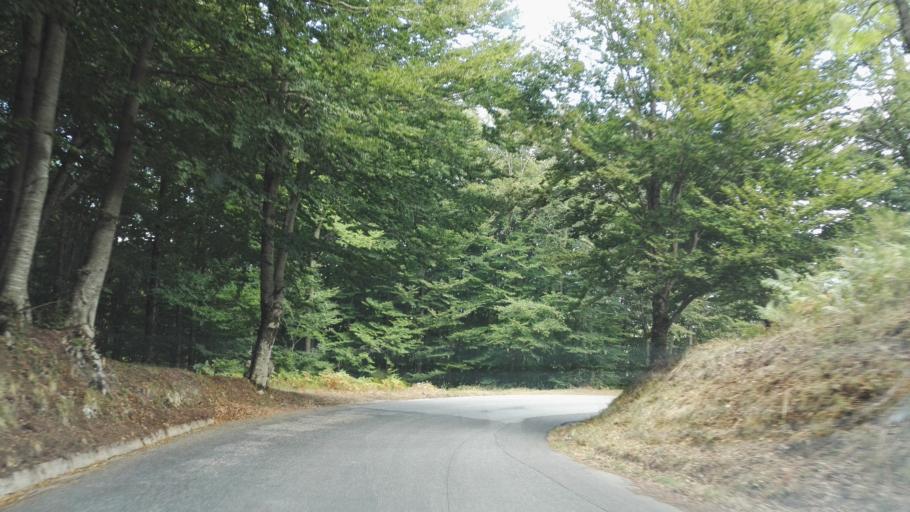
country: IT
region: Calabria
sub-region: Provincia di Vibo-Valentia
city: Nardodipace
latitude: 38.4919
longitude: 16.3473
